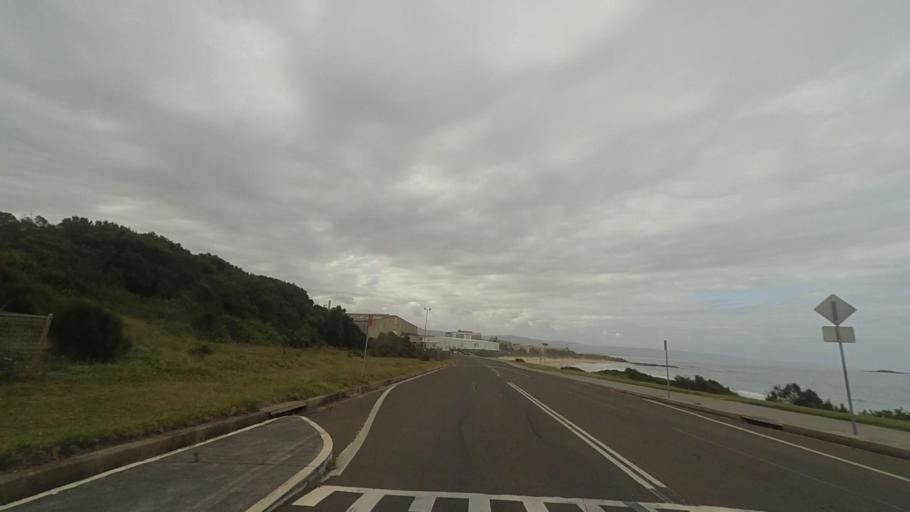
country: AU
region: New South Wales
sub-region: Wollongong
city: Port Kembla
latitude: -34.4848
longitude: 150.9148
